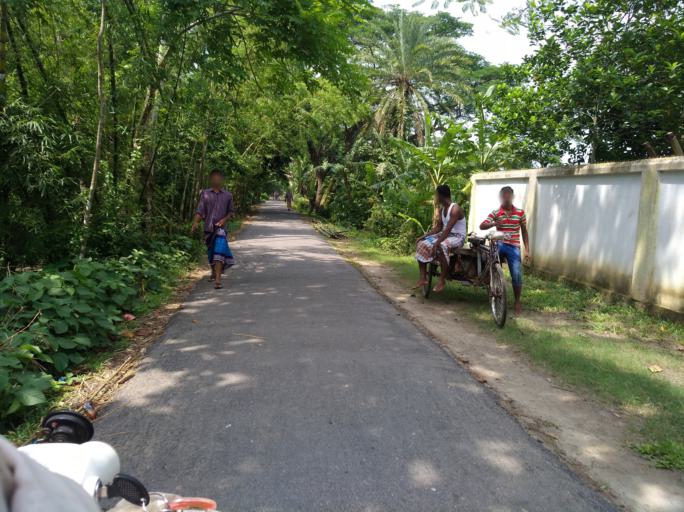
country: BD
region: Dhaka
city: Palang
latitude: 23.2529
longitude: 90.3109
